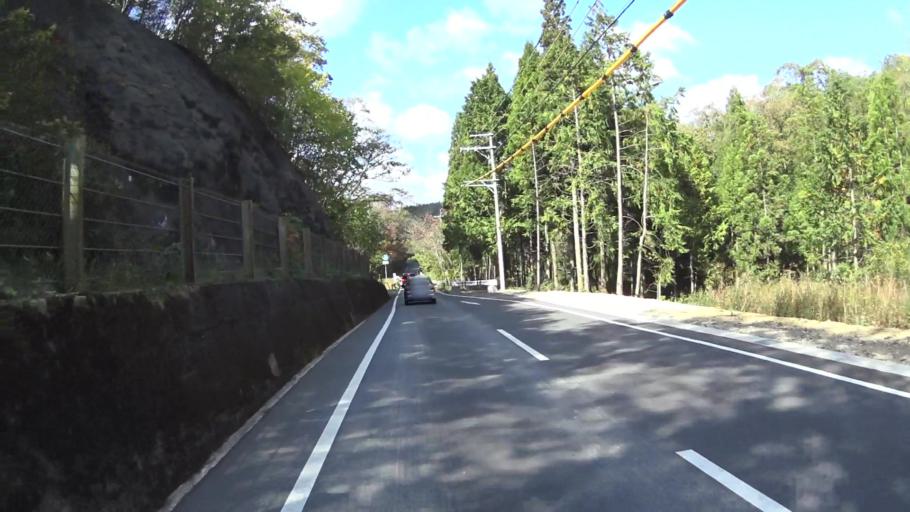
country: JP
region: Kyoto
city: Kameoka
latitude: 35.1644
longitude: 135.4582
